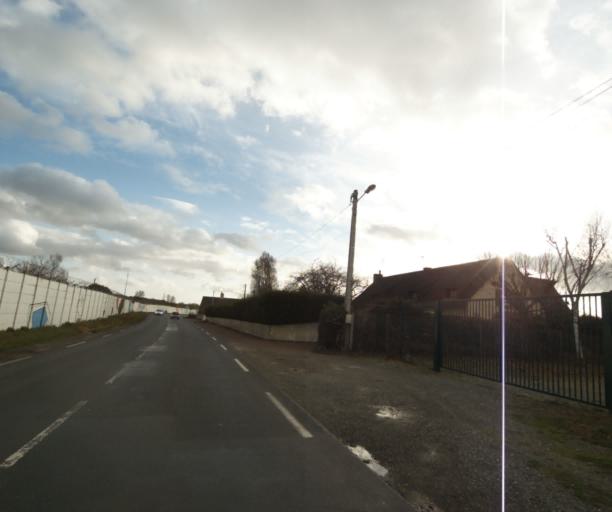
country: FR
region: Pays de la Loire
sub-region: Departement de la Sarthe
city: Arnage
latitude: 47.9408
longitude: 0.2077
